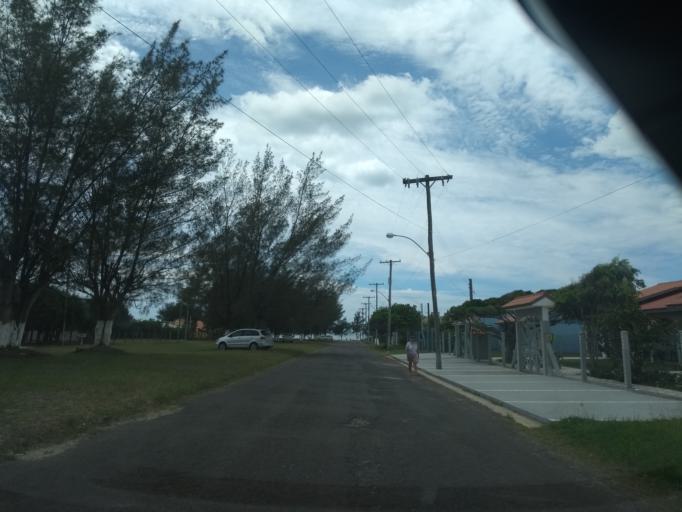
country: BR
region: Rio Grande do Sul
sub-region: Tramandai
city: Tramandai
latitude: -30.0627
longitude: -50.1617
